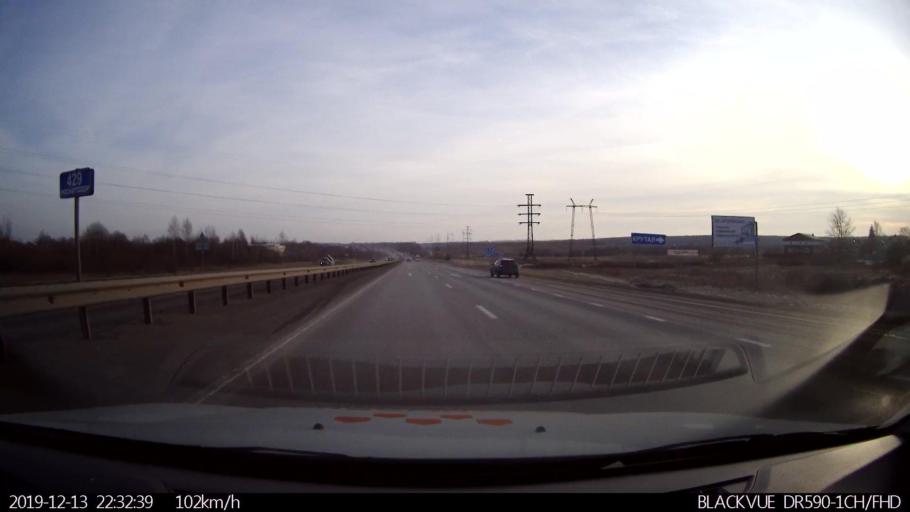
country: RU
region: Nizjnij Novgorod
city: Afonino
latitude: 56.2037
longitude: 44.0953
